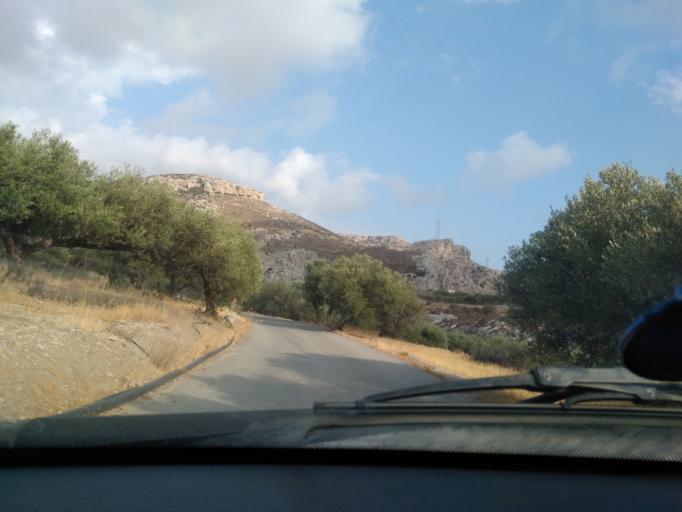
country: GR
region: Crete
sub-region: Nomos Lasithiou
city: Makry-Gialos
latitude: 35.0450
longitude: 26.0556
